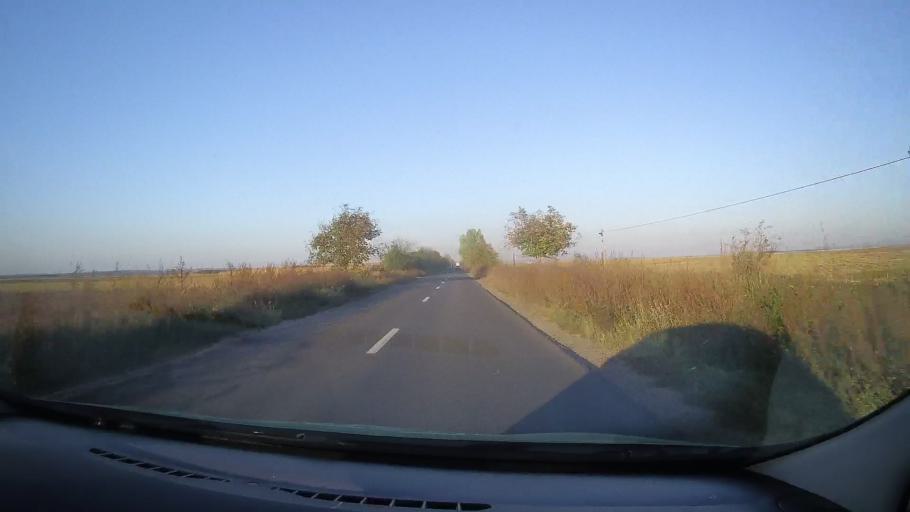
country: RO
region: Bihor
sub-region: Comuna Salard
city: Salard
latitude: 47.1921
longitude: 21.9966
